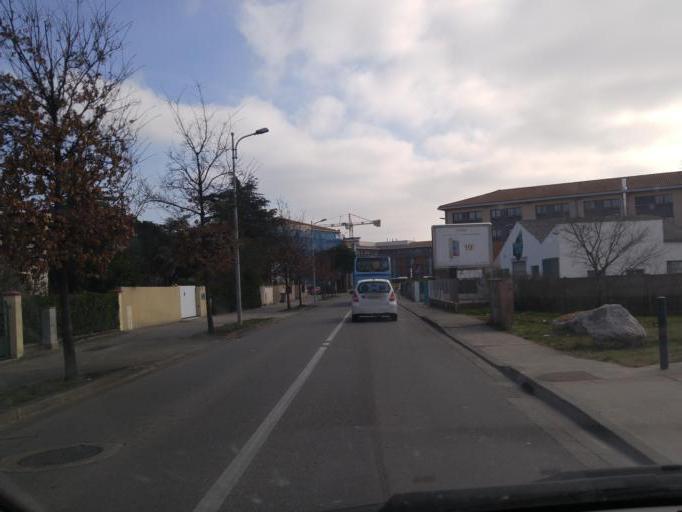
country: FR
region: Midi-Pyrenees
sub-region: Departement de la Haute-Garonne
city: Blagnac
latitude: 43.6404
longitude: 1.3760
